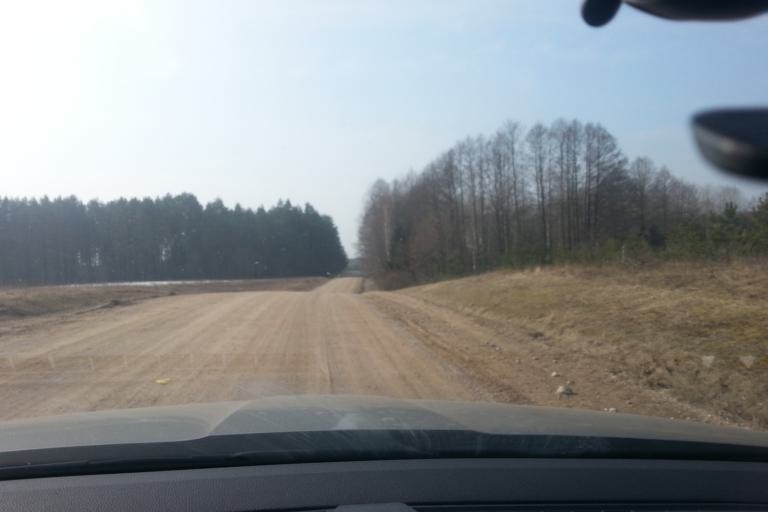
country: LT
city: Trakai
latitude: 54.5218
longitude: 24.9472
